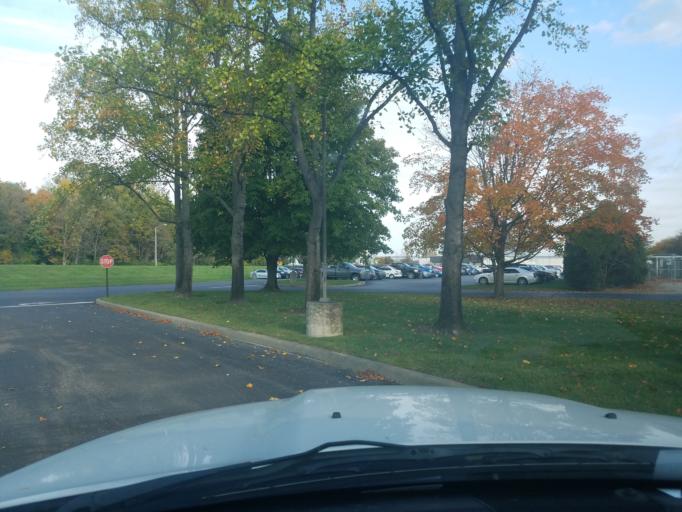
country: US
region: Indiana
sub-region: Jackson County
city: Seymour
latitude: 38.9675
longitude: -85.8616
